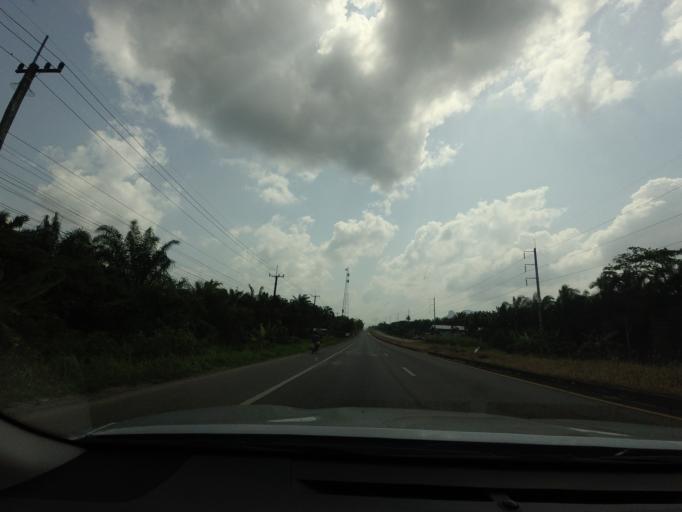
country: TH
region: Phangnga
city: Thap Put
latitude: 8.5020
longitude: 98.6977
